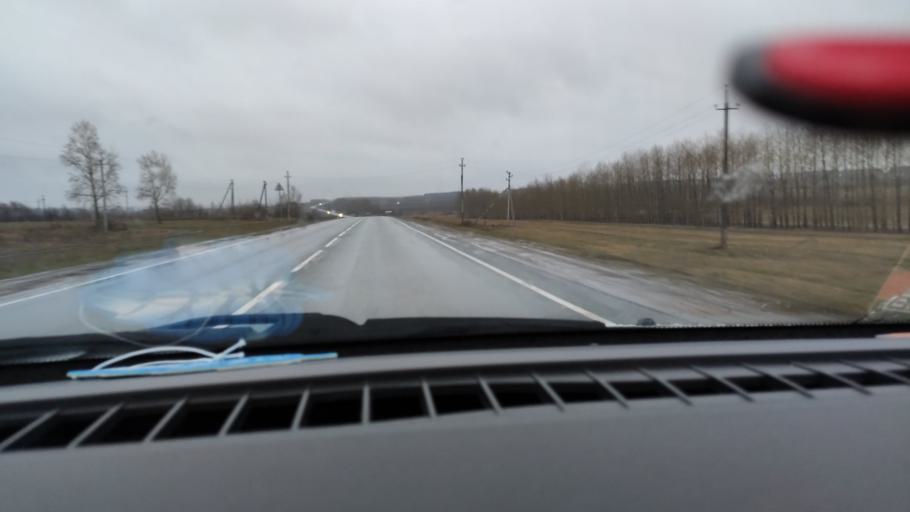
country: RU
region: Tatarstan
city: Mendeleyevsk
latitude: 55.9730
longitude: 52.3190
